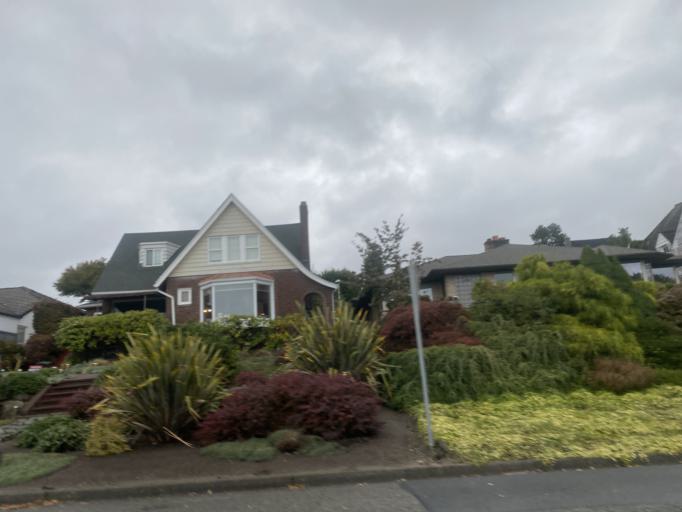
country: US
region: Washington
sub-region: King County
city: Seattle
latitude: 47.6415
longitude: -122.4134
